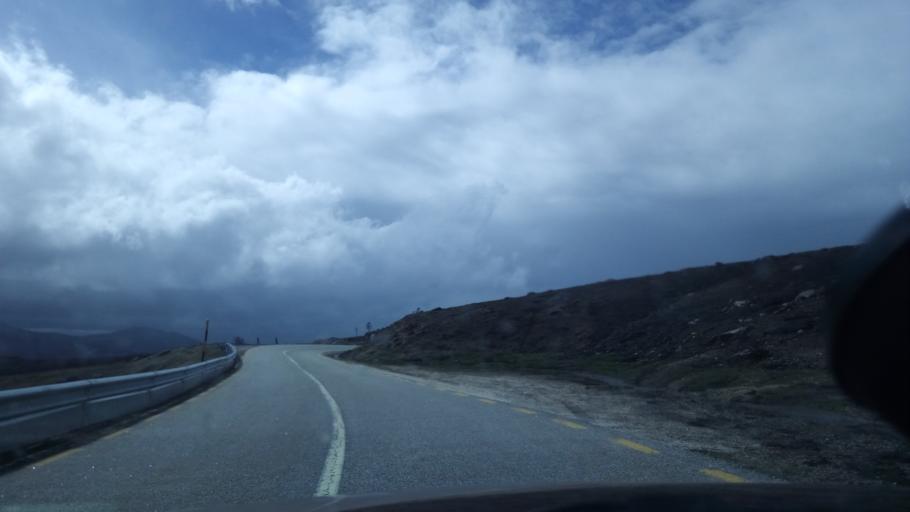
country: PT
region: Guarda
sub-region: Manteigas
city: Manteigas
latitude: 40.4190
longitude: -7.6076
